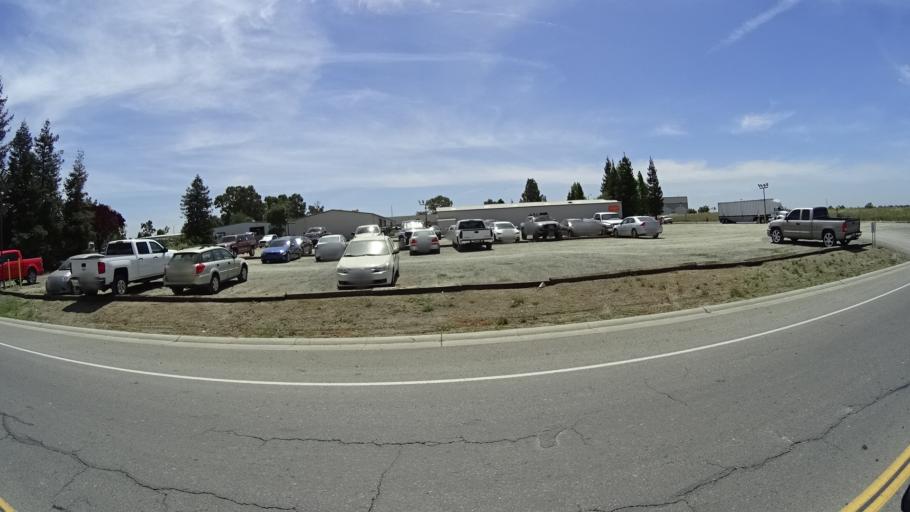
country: US
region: California
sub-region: Placer County
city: Roseville
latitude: 38.8173
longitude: -121.3113
